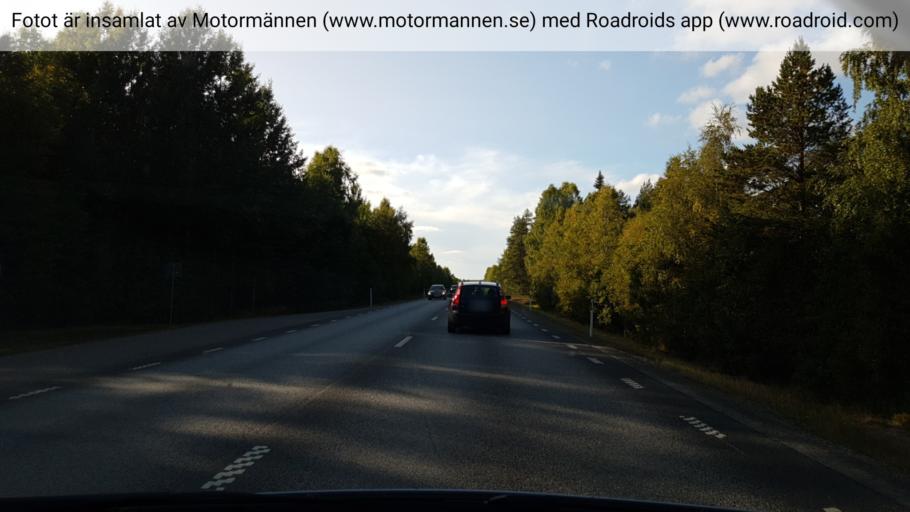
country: SE
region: Vaesterbotten
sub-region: Umea Kommun
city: Roback
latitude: 63.8512
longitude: 20.1136
